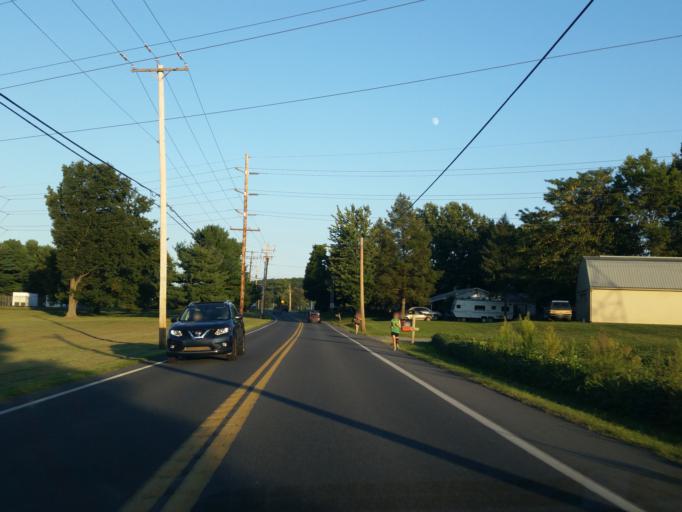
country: US
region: Pennsylvania
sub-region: Lebanon County
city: Sand Hill
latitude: 40.3752
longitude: -76.4388
